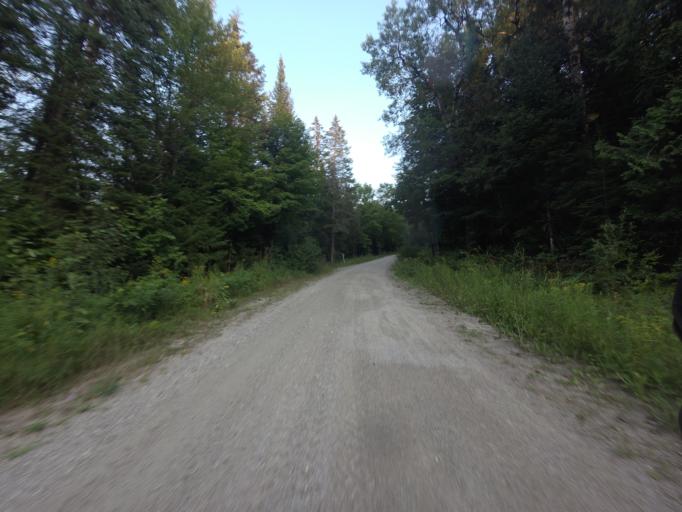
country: CA
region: Ontario
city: Renfrew
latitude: 45.0776
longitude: -76.7225
